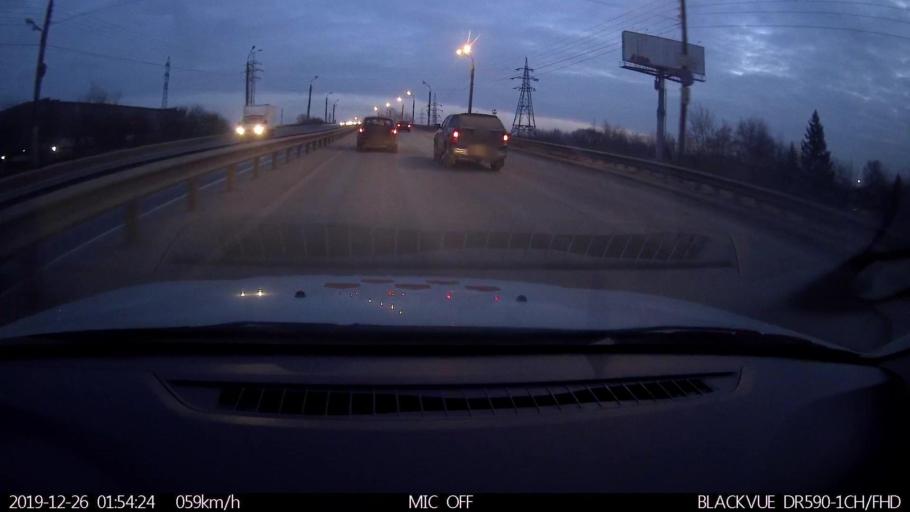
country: RU
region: Nizjnij Novgorod
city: Nizhniy Novgorod
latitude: 56.3087
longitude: 43.9015
